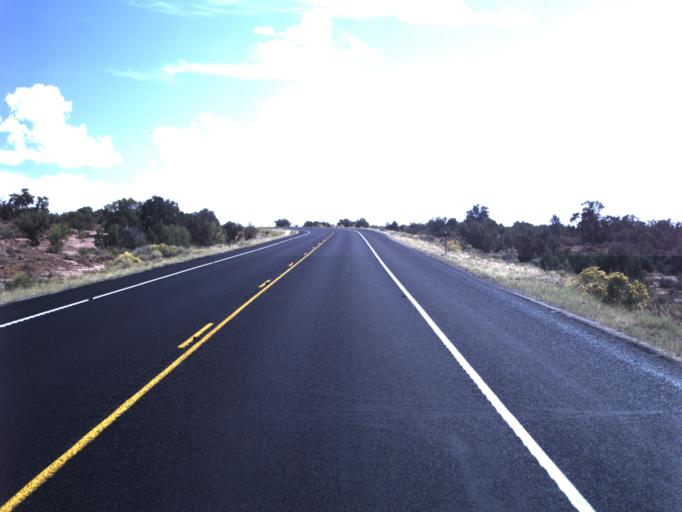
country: US
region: Utah
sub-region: Grand County
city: Moab
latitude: 38.6070
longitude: -109.8172
